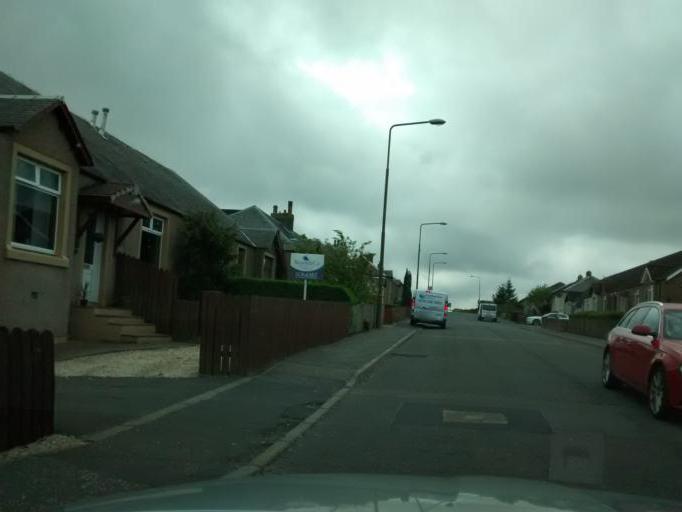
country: GB
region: Scotland
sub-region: North Lanarkshire
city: Harthill
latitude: 55.8791
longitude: -3.7595
